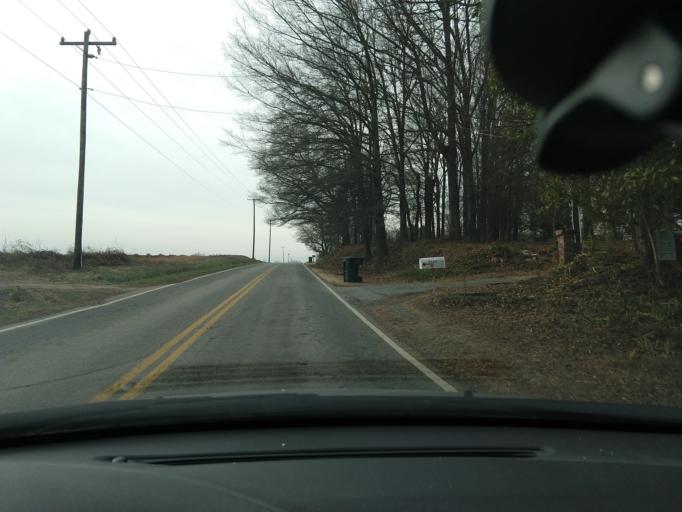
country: US
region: South Carolina
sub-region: Spartanburg County
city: Cowpens
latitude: 35.0688
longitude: -81.7630
